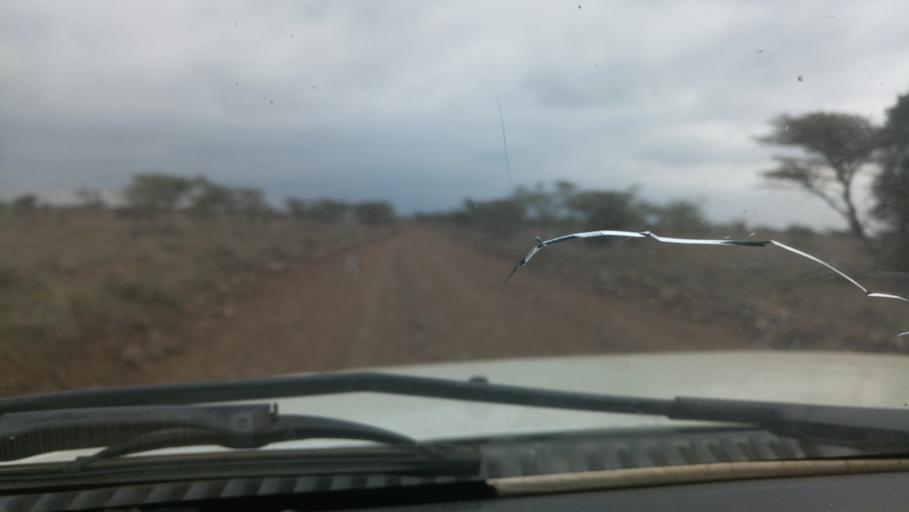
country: KE
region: Nairobi Area
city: Pumwani
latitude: -1.3846
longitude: 36.8450
